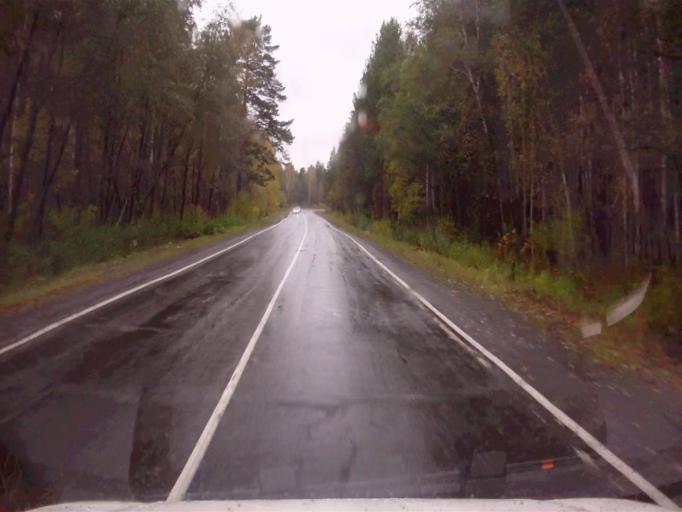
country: RU
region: Chelyabinsk
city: Verkhniy Ufaley
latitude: 55.9587
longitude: 60.3878
